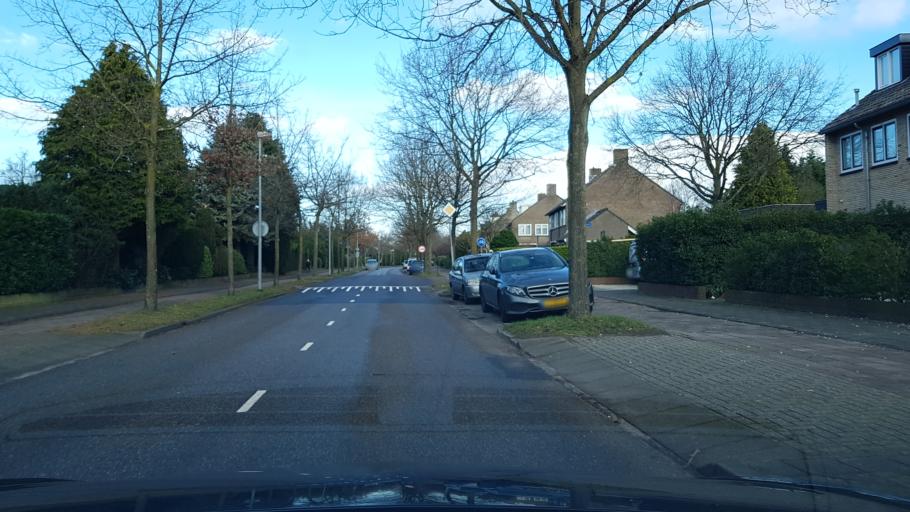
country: NL
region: North Holland
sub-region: Gemeente Bussum
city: Bussum
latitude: 52.2809
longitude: 5.1474
